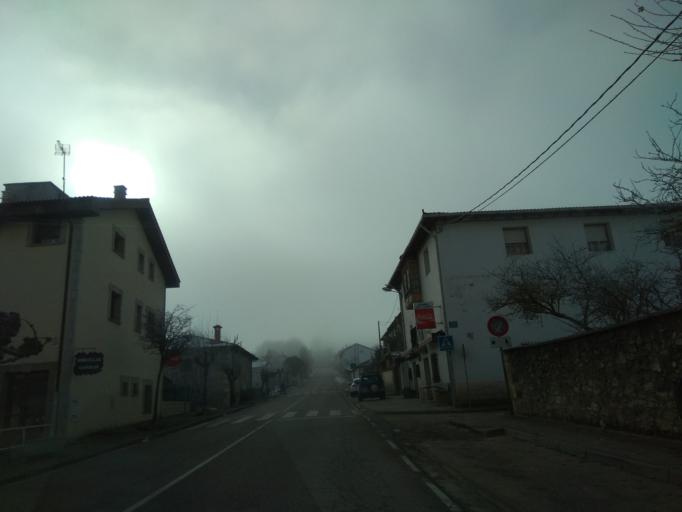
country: ES
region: Castille and Leon
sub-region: Provincia de Burgos
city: Espinosa de los Monteros
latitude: 43.0071
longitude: -3.5199
